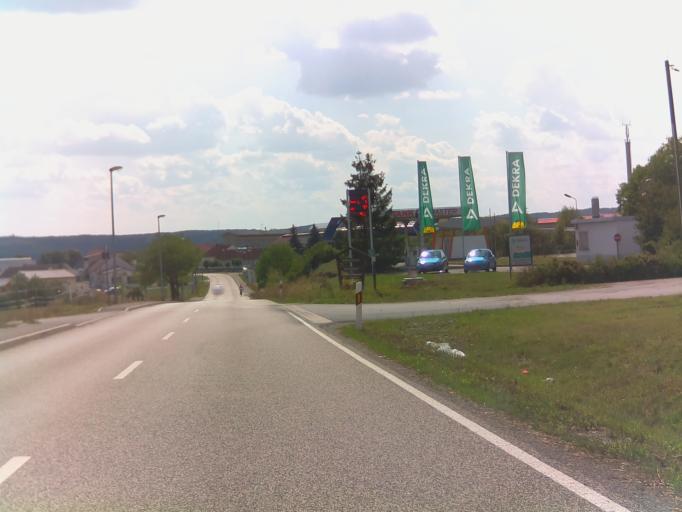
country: DE
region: Thuringia
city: Westhausen
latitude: 50.3632
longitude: 10.6921
